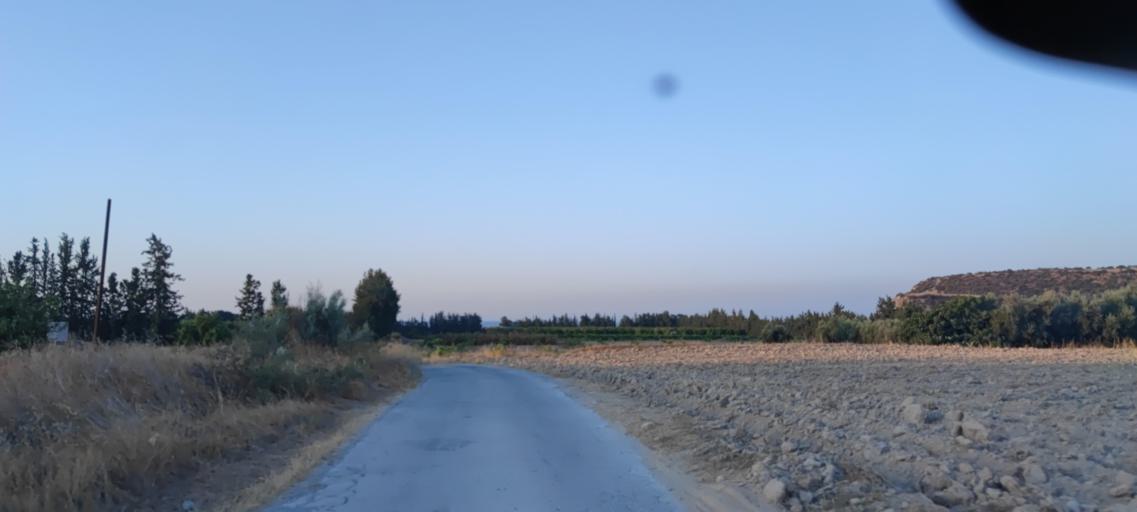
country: CY
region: Limassol
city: Sotira
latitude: 34.6741
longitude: 32.7959
